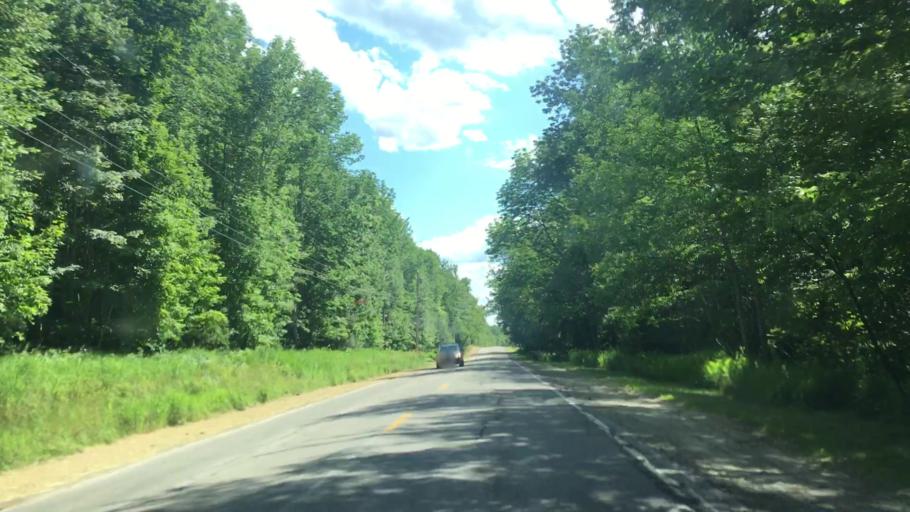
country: US
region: Maine
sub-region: Franklin County
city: Farmington
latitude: 44.6997
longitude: -70.1118
